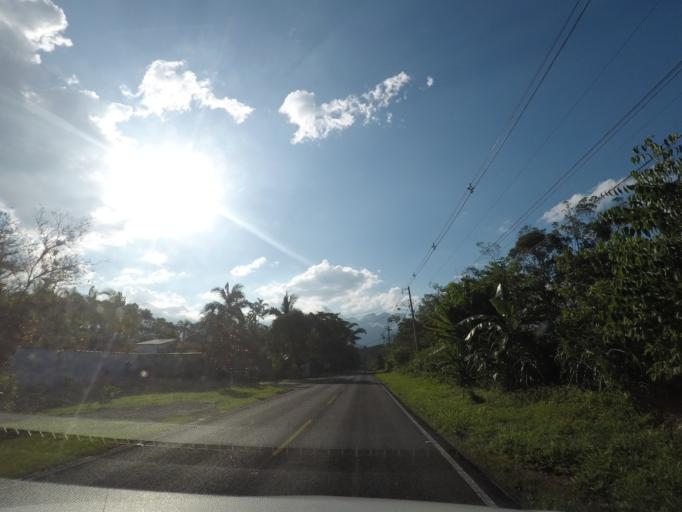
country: BR
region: Parana
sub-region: Antonina
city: Antonina
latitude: -25.4318
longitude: -48.8734
